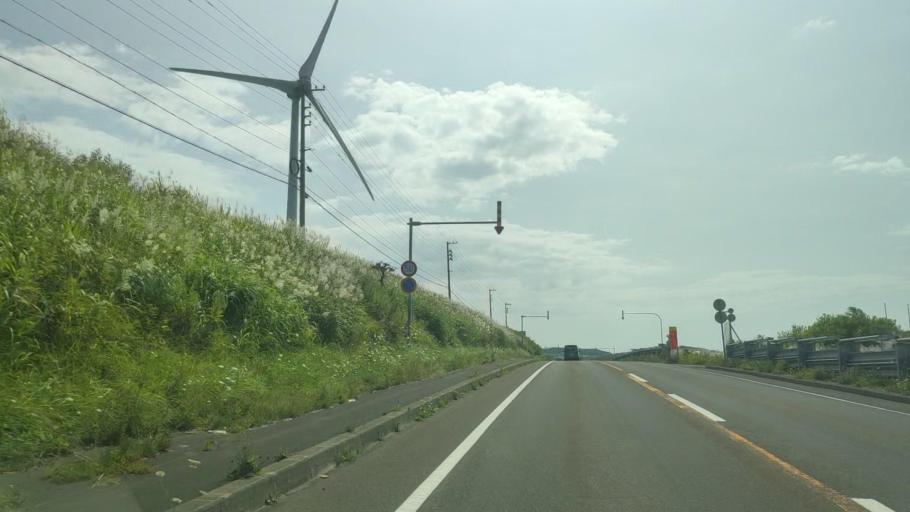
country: JP
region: Hokkaido
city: Rumoi
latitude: 44.3183
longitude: 141.6662
